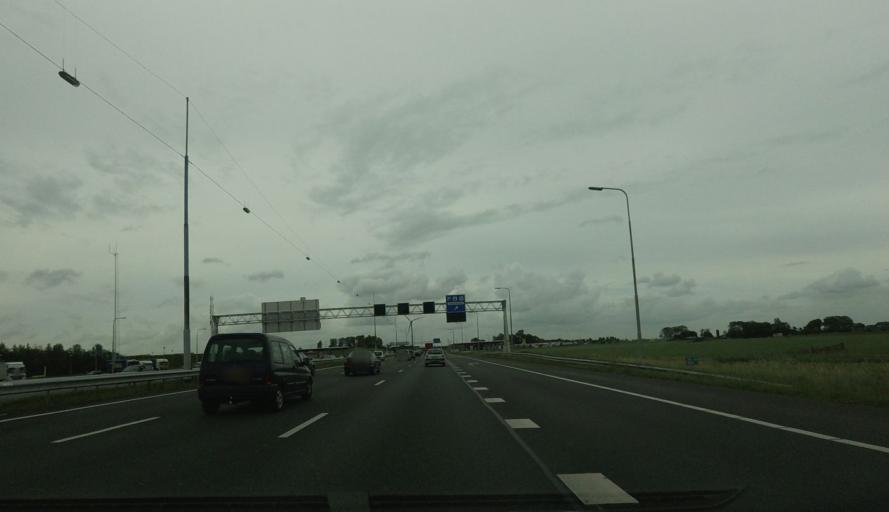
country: NL
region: North Holland
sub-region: Gemeente Heemskerk
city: Heemskerk
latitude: 52.4966
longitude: 4.6996
